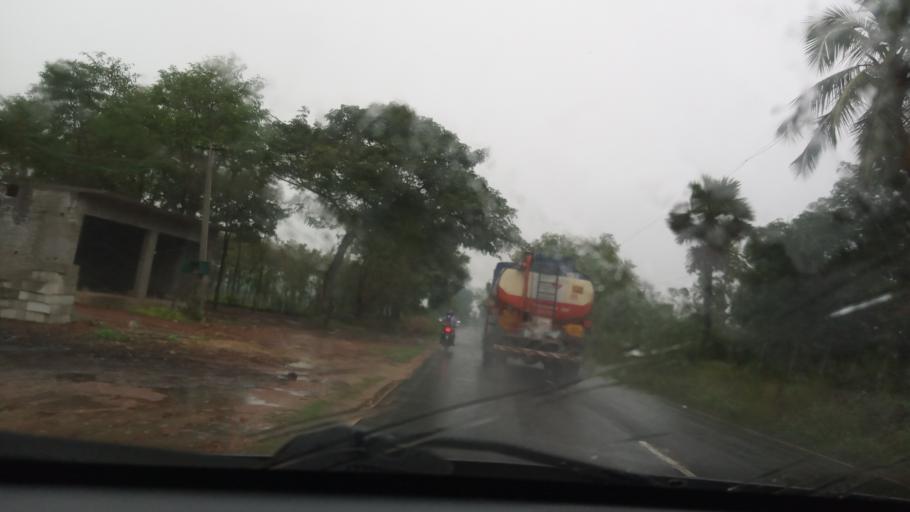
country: IN
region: Tamil Nadu
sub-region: Vellore
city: Kalavai
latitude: 12.8203
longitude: 79.4104
